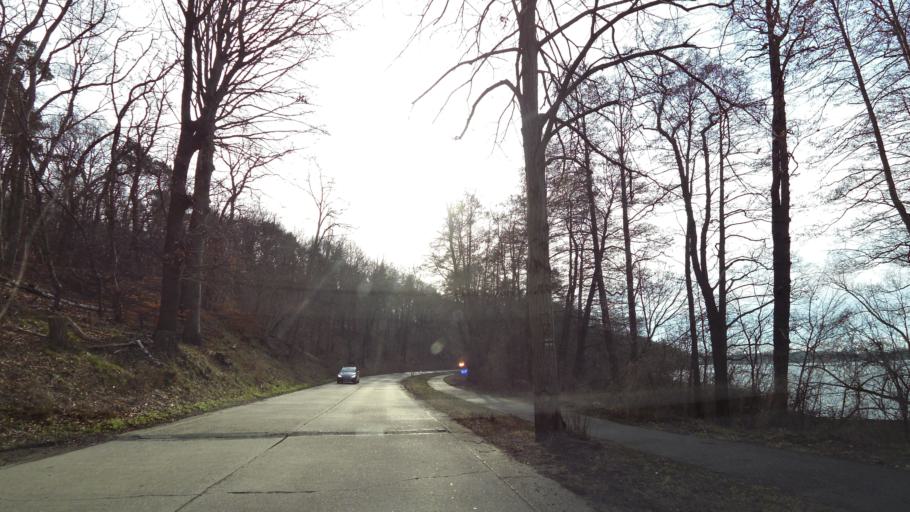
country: DE
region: Brandenburg
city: Michendorf
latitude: 52.3583
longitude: 13.0215
